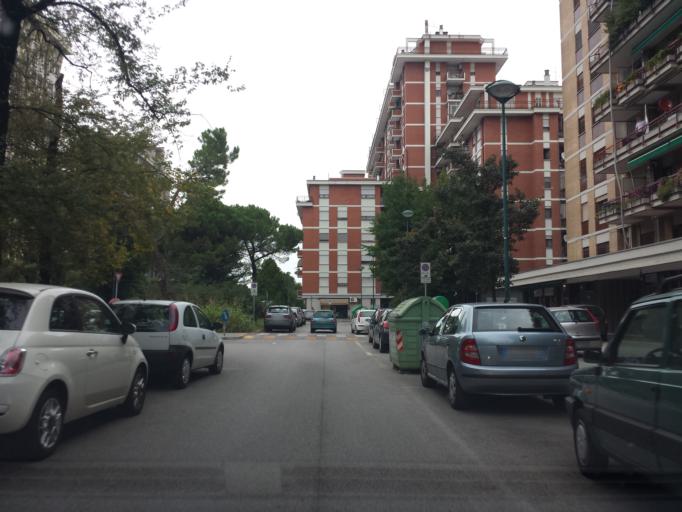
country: IT
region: Veneto
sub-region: Provincia di Venezia
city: Mestre
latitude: 45.4806
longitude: 12.2246
